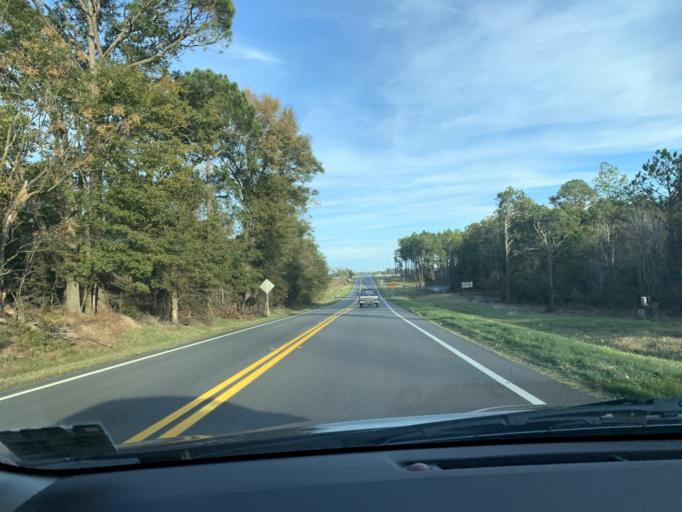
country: US
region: Georgia
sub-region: Irwin County
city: Ocilla
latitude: 31.5937
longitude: -83.1918
